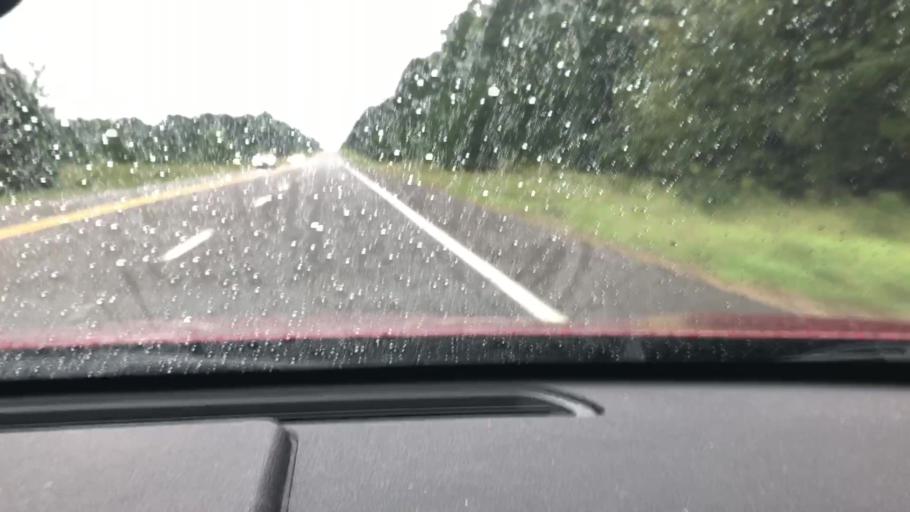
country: US
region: Arkansas
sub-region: Columbia County
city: Waldo
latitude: 33.3094
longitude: -93.2790
